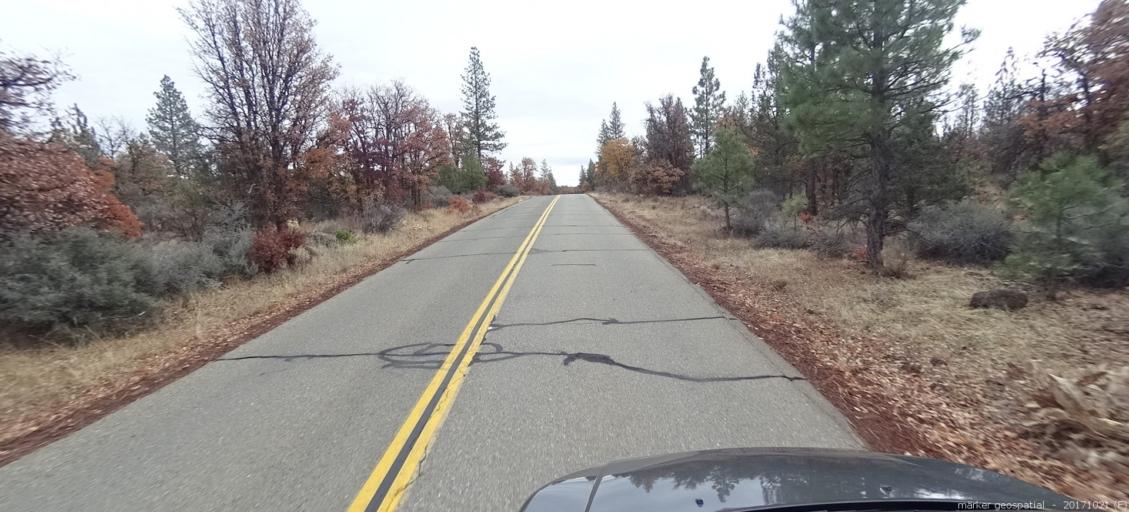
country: US
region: California
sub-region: Shasta County
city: Burney
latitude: 40.9323
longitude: -121.5603
